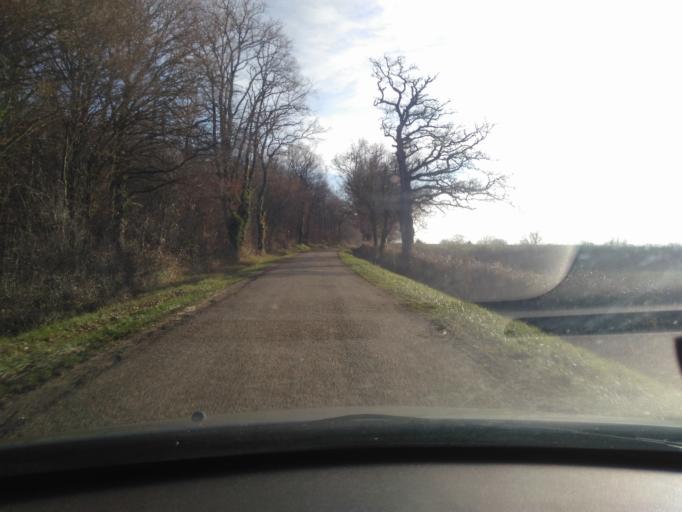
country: FR
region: Bourgogne
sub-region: Departement de la Nievre
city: Magny-Cours
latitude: 46.8669
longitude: 3.1594
